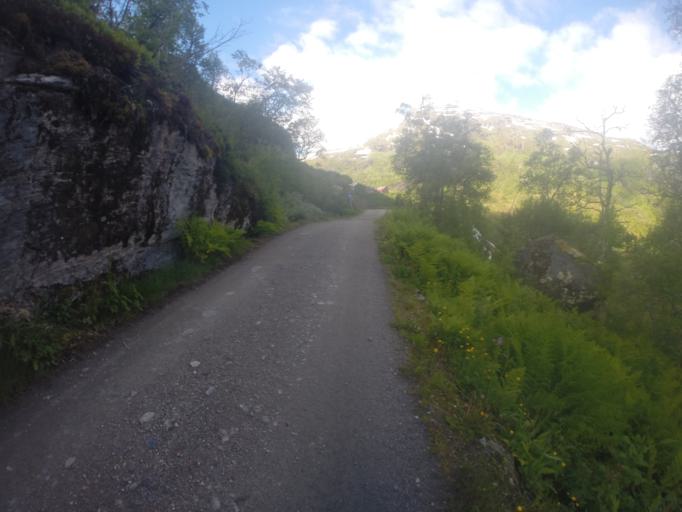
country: NO
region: Sogn og Fjordane
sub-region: Aurland
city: Aurlandsvangen
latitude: 60.7422
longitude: 7.1278
